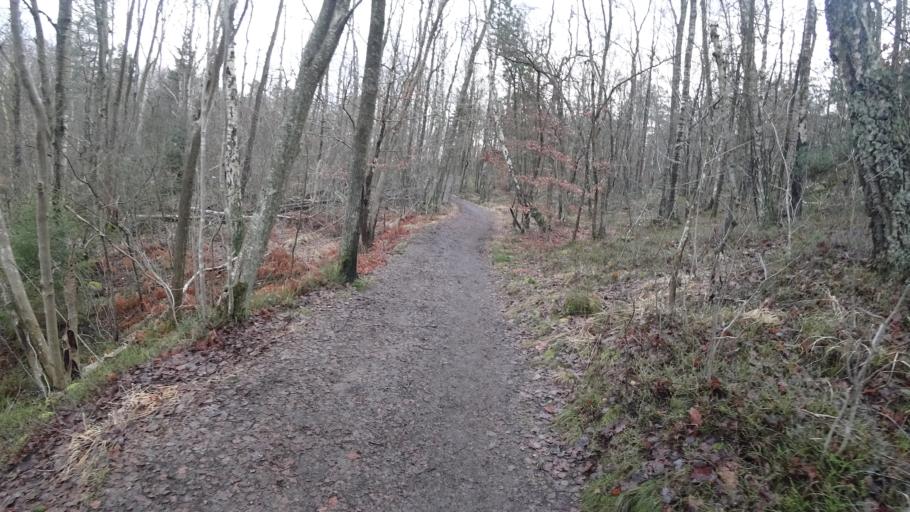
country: SE
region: Vaestra Goetaland
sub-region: Goteborg
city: Goeteborg
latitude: 57.6679
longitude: 11.9512
